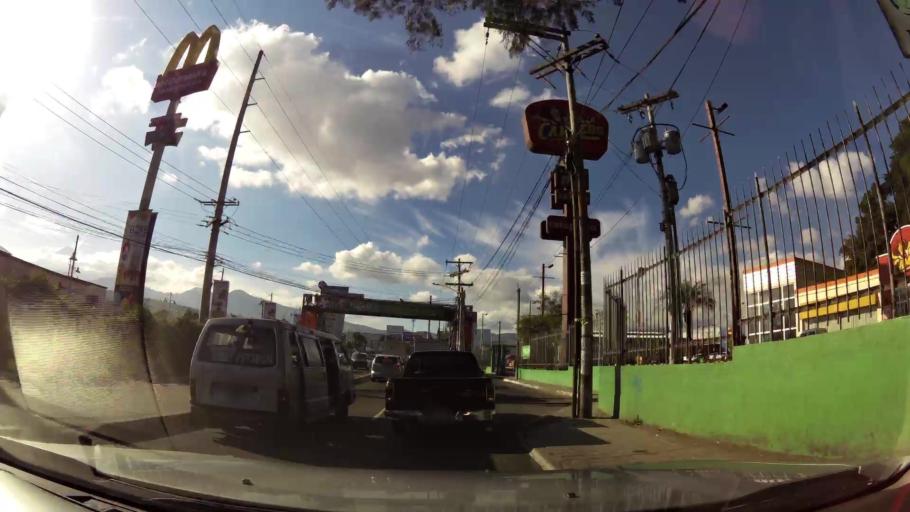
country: GT
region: Guatemala
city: Villa Nueva
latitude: 14.5147
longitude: -90.5756
